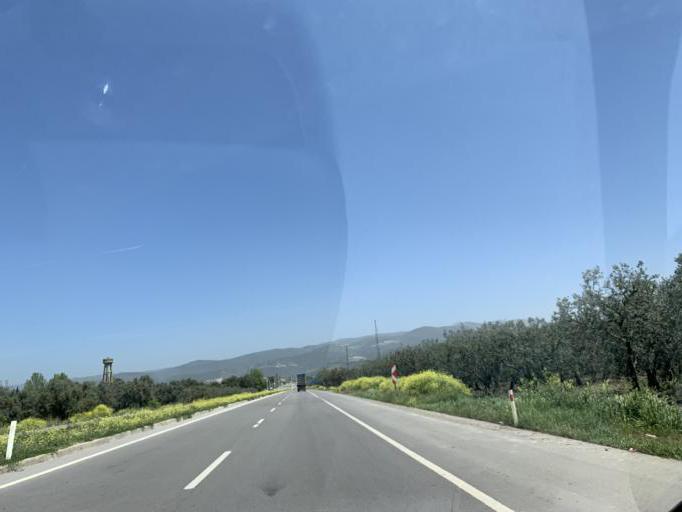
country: TR
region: Bursa
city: Iznik
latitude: 40.4027
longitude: 29.6993
